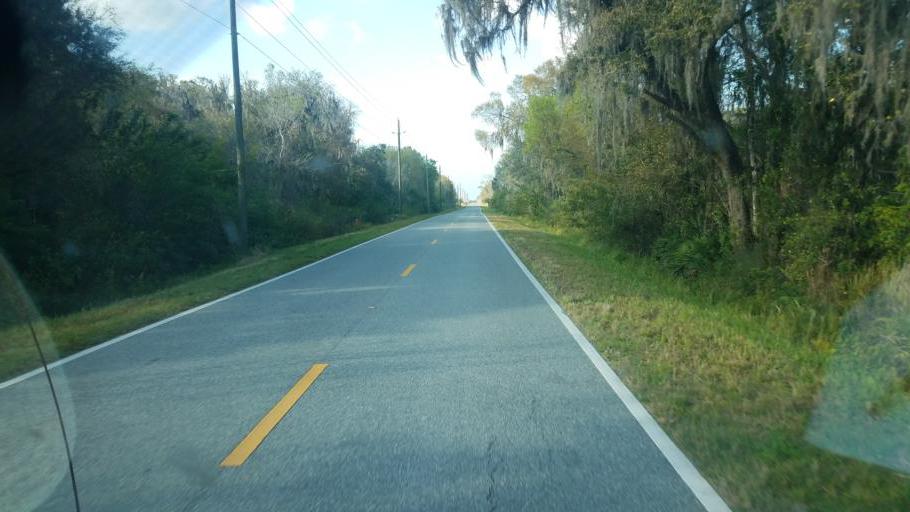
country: US
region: Florida
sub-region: Hardee County
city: Bowling Green
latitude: 27.6383
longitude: -81.9476
